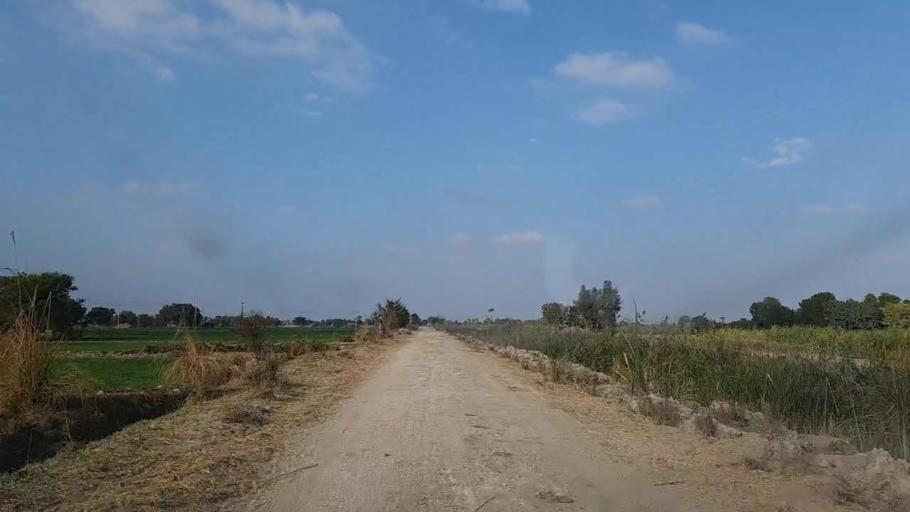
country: PK
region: Sindh
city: Sanghar
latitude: 26.2343
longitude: 68.9729
